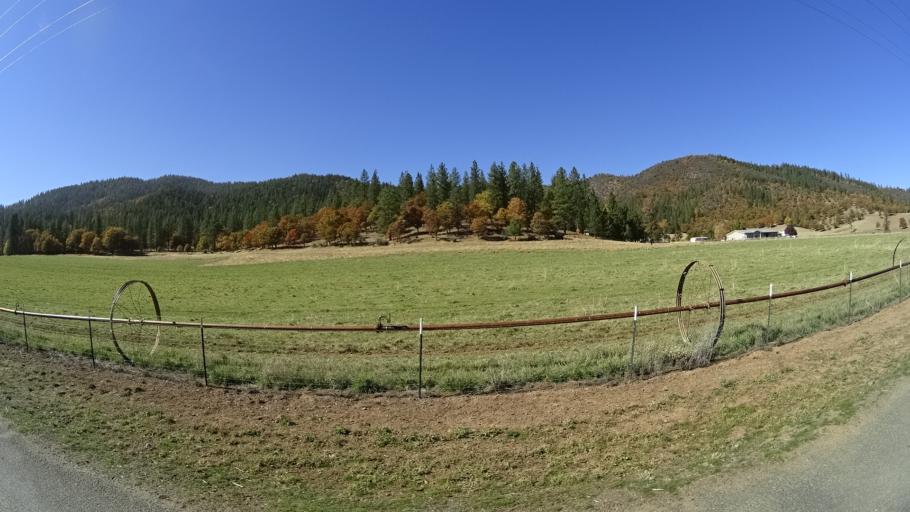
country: US
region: California
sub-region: Siskiyou County
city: Yreka
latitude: 41.6054
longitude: -122.9080
